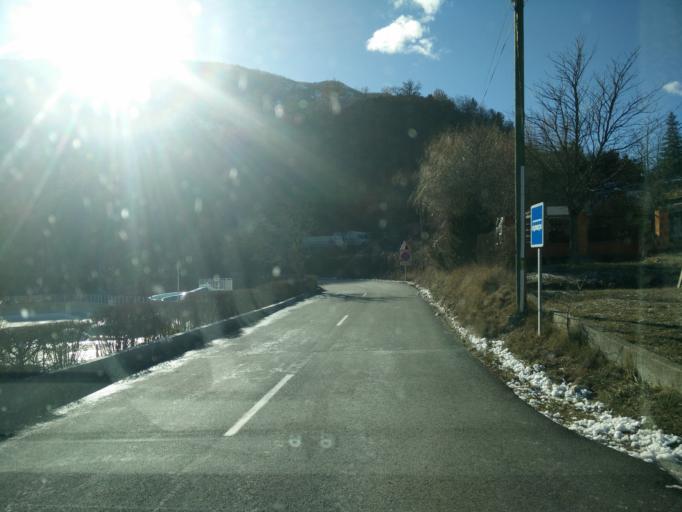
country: FR
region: Provence-Alpes-Cote d'Azur
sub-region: Departement des Alpes-de-Haute-Provence
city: Castellane
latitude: 43.8392
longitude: 6.4937
